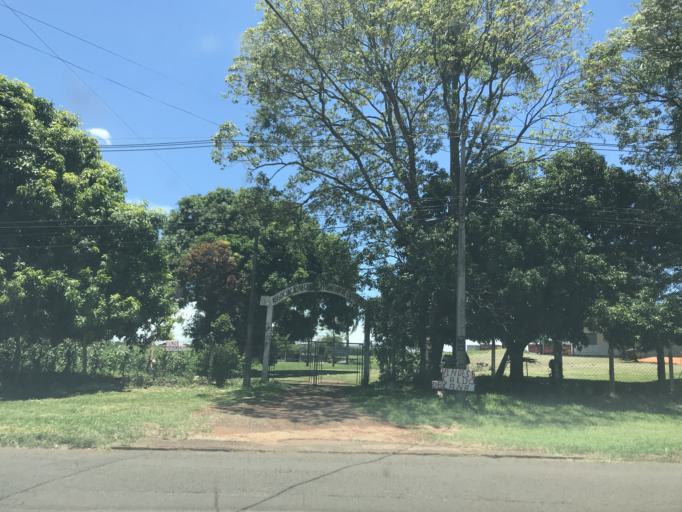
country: BR
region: Parana
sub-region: Sarandi
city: Sarandi
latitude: -23.4373
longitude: -51.8964
